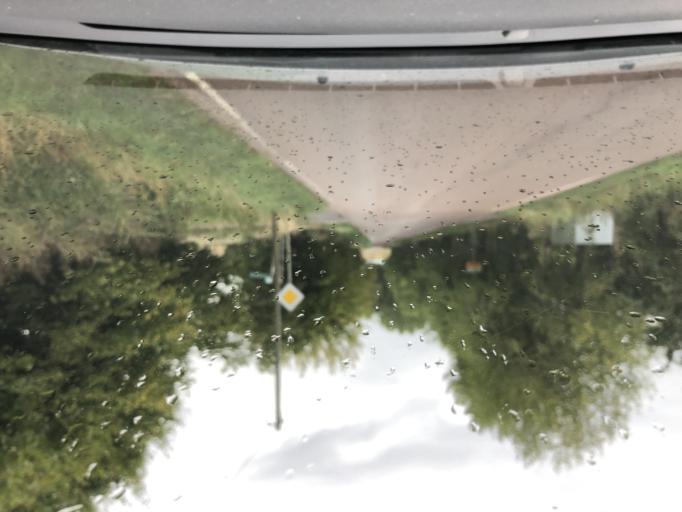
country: DE
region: Saxony-Anhalt
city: Wulfen
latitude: 51.8183
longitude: 11.9065
